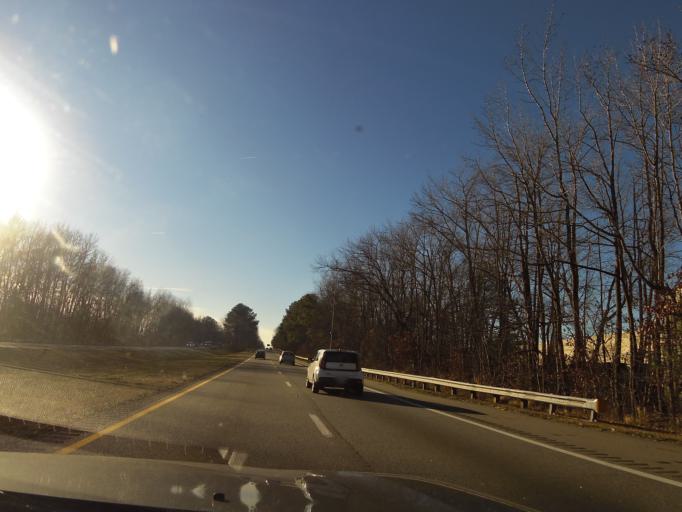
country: US
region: Virginia
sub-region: City of Suffolk
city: Suffolk
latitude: 36.7659
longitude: -76.5452
